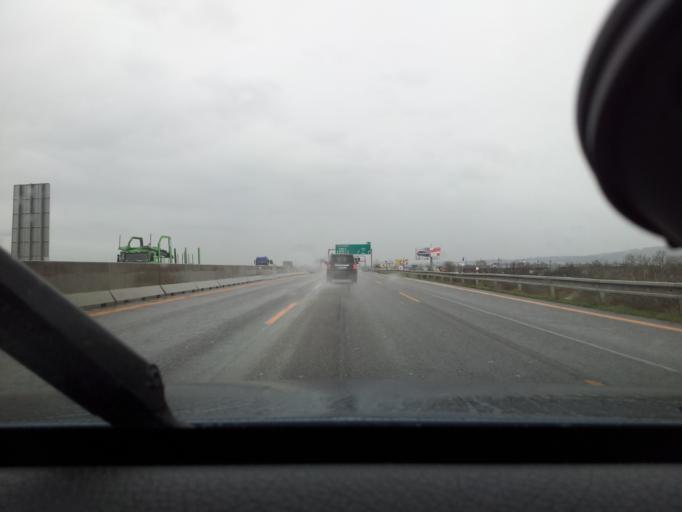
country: SK
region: Bratislavsky
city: Svaty Jur
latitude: 48.1976
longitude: 17.2249
